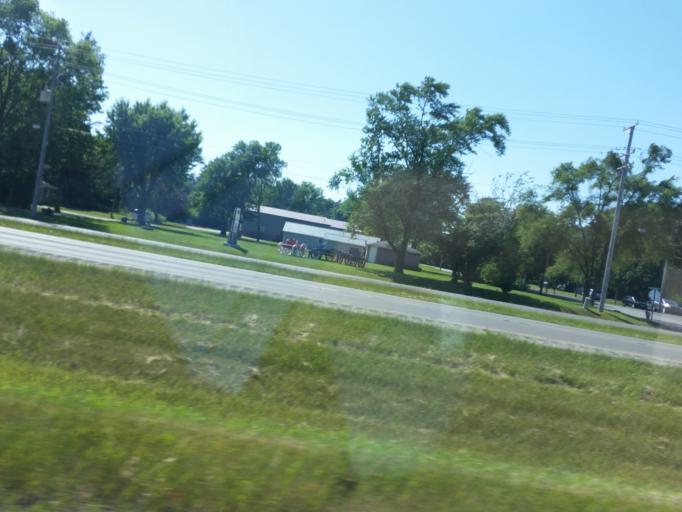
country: US
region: Illinois
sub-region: Winnebago County
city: Roscoe
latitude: 42.3869
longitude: -89.0186
